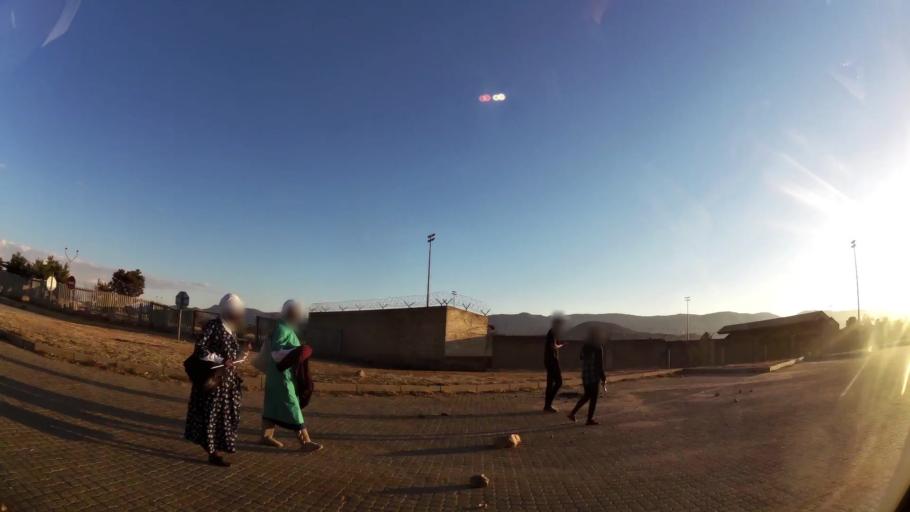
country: ZA
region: Limpopo
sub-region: Waterberg District Municipality
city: Mokopane
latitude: -24.1421
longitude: 28.9888
